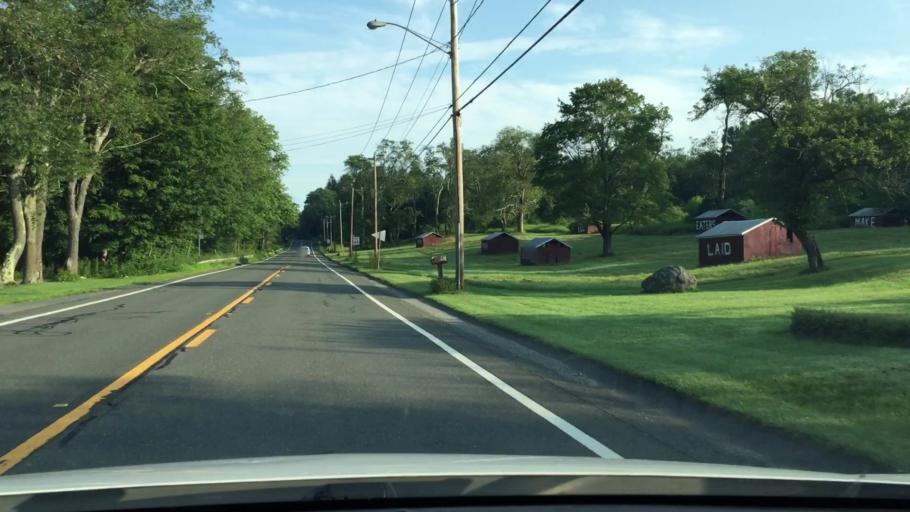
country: US
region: Massachusetts
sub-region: Berkshire County
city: Otis
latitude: 42.2331
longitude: -73.1107
